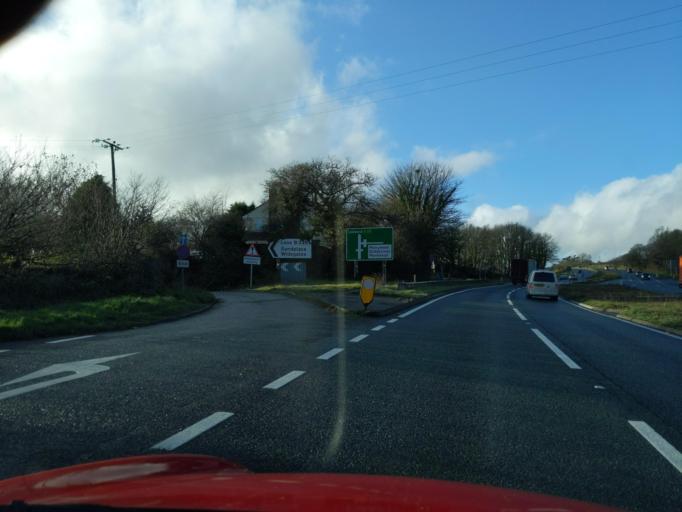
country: GB
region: England
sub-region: Cornwall
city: Liskeard
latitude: 50.4226
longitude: -4.4091
